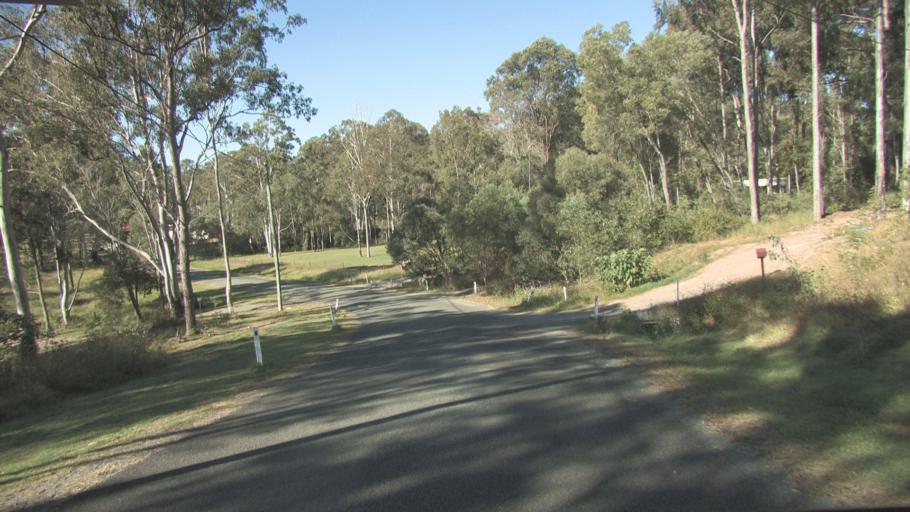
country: AU
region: Queensland
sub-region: Logan
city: Windaroo
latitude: -27.7618
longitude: 153.1472
